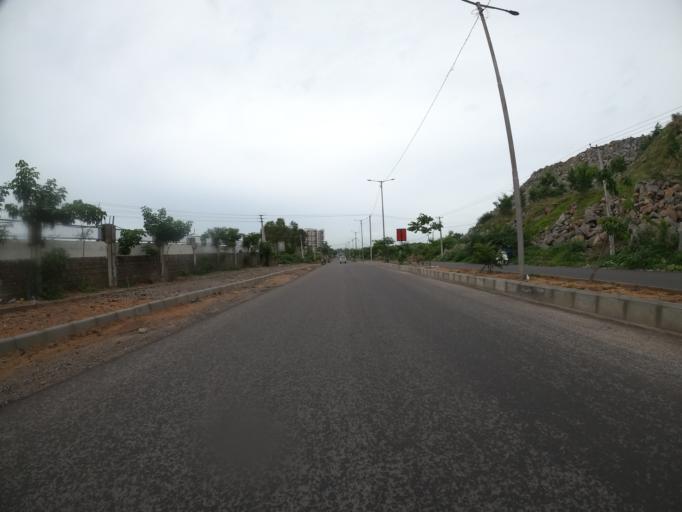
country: IN
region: Telangana
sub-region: Rangareddi
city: Kukatpalli
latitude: 17.4628
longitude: 78.3870
